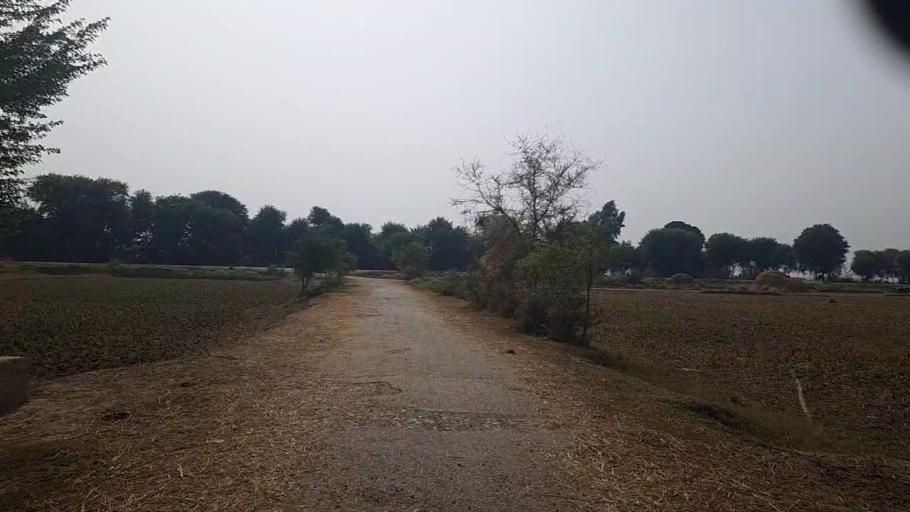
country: PK
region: Sindh
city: Kashmor
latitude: 28.3787
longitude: 69.4463
